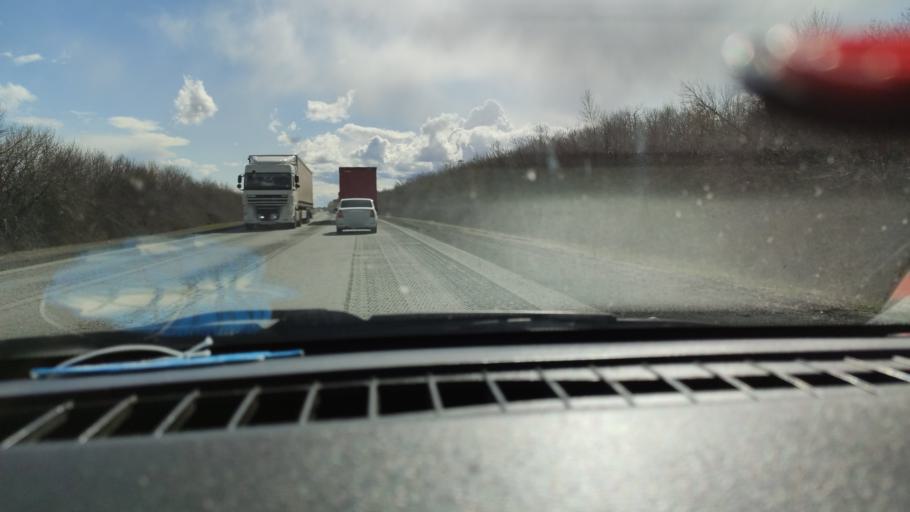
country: RU
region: Saratov
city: Dukhovnitskoye
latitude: 52.6463
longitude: 48.1961
